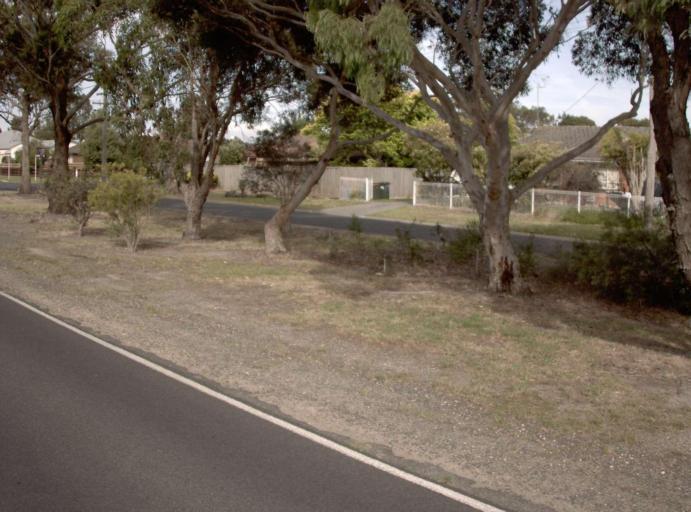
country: AU
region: Victoria
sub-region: Latrobe
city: Traralgon
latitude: -38.1225
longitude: 146.5716
